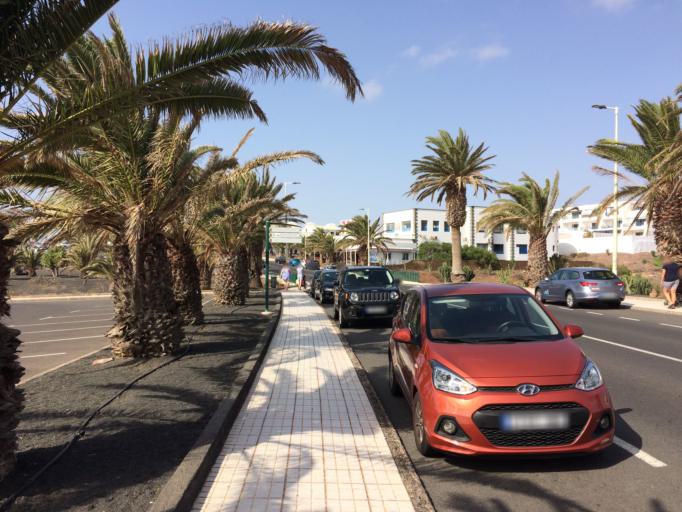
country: ES
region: Canary Islands
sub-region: Provincia de Las Palmas
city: Arrecife
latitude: 29.0012
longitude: -13.4887
